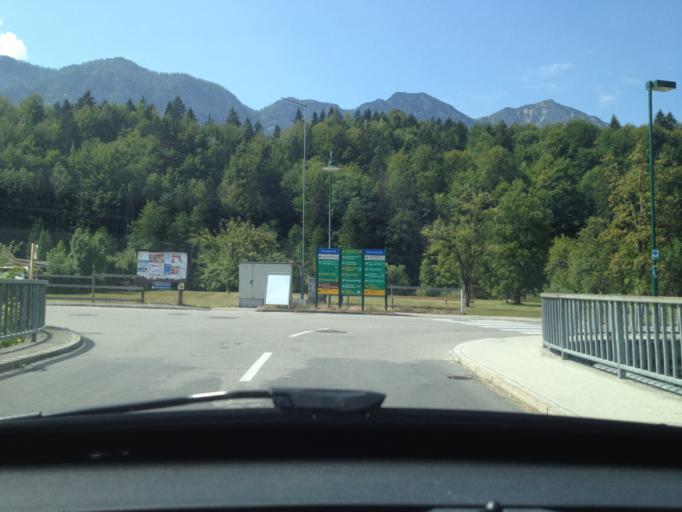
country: AT
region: Upper Austria
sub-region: Politischer Bezirk Gmunden
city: Bad Goisern
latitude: 47.6371
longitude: 13.6154
